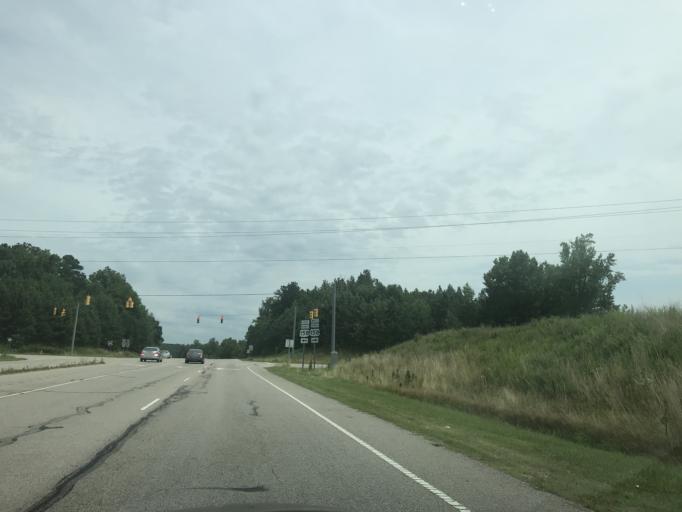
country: US
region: North Carolina
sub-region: Vance County
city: South Henderson
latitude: 36.3075
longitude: -78.4425
